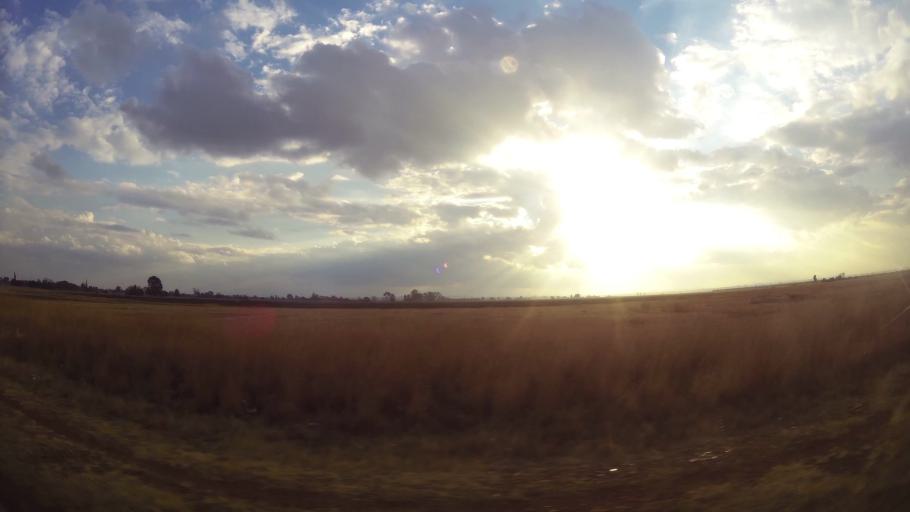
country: ZA
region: Gauteng
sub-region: Sedibeng District Municipality
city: Vanderbijlpark
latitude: -26.6254
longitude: 27.8106
